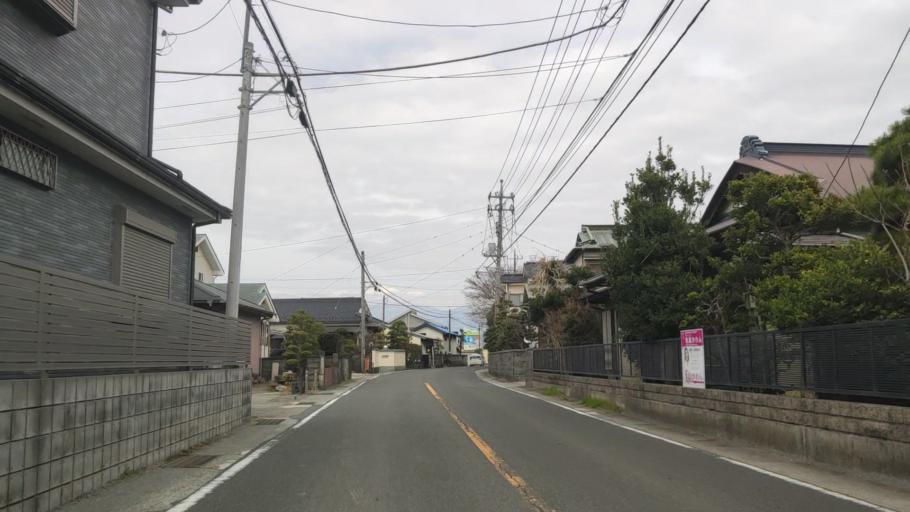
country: JP
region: Kanagawa
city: Ninomiya
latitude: 35.2952
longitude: 139.2331
